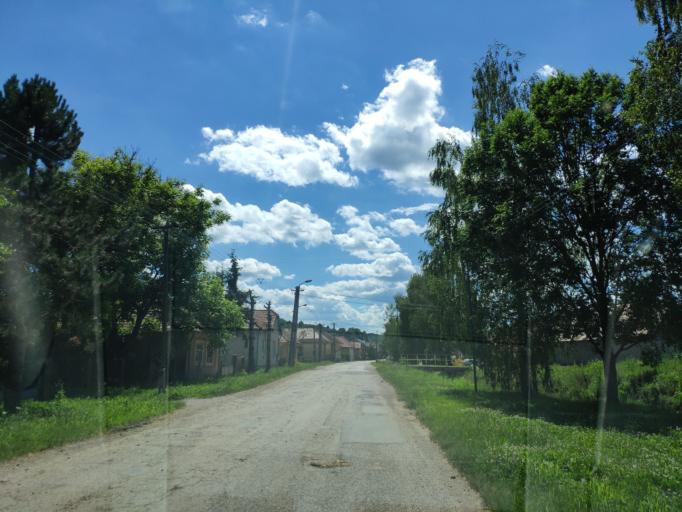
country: HU
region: Borsod-Abauj-Zemplen
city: Arlo
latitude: 48.2814
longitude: 20.1907
